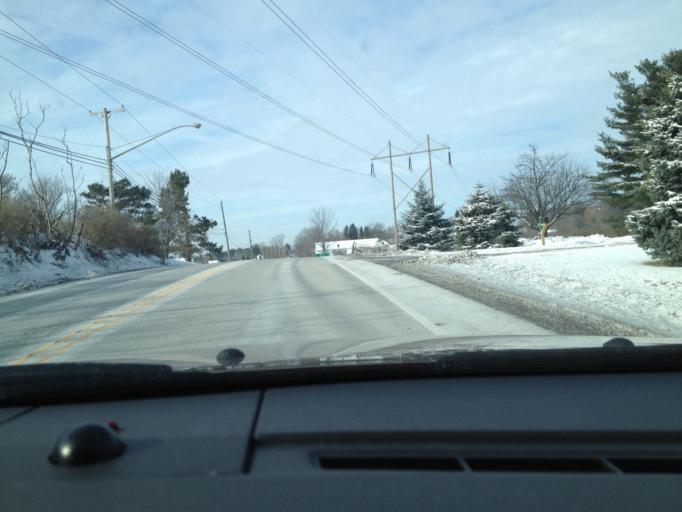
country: US
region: New York
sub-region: Rensselaer County
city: West Sand Lake
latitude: 42.6425
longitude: -73.6225
